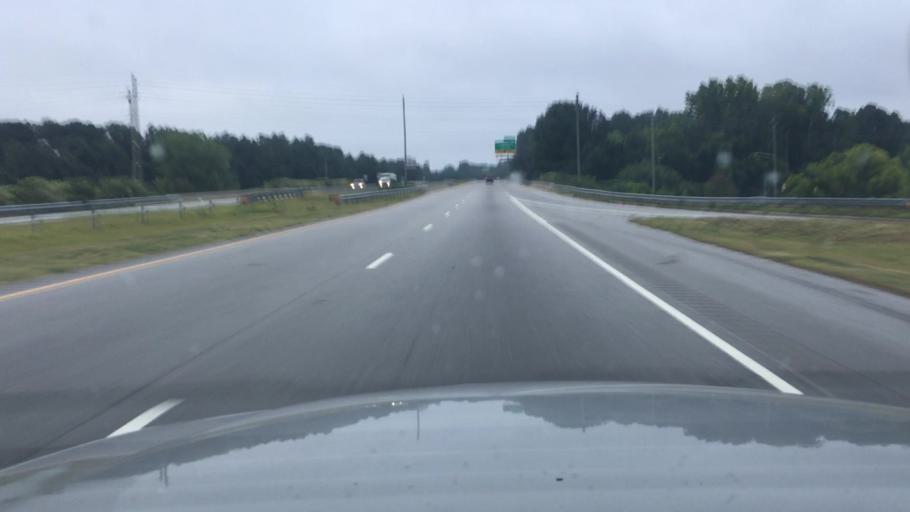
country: US
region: North Carolina
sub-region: Cumberland County
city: Fayetteville
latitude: 35.0457
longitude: -78.8934
